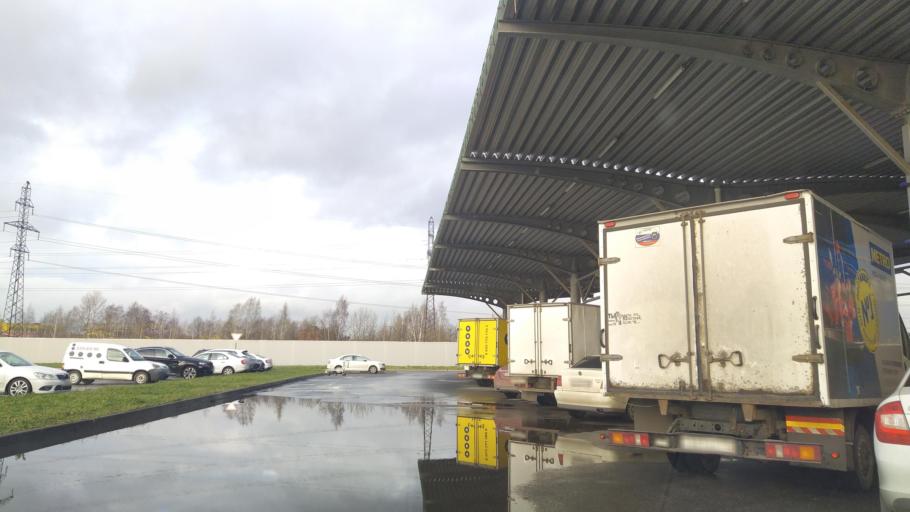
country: RU
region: St.-Petersburg
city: Krasnogvargeisky
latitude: 59.9406
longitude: 30.4547
